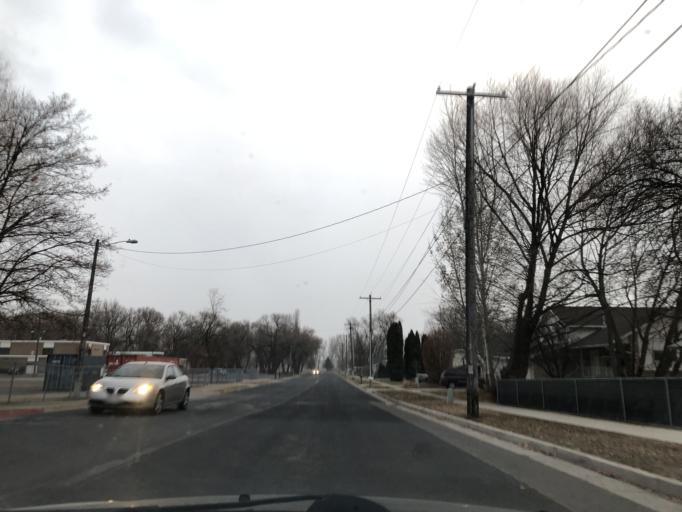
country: US
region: Utah
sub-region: Cache County
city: Logan
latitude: 41.7222
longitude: -111.8489
